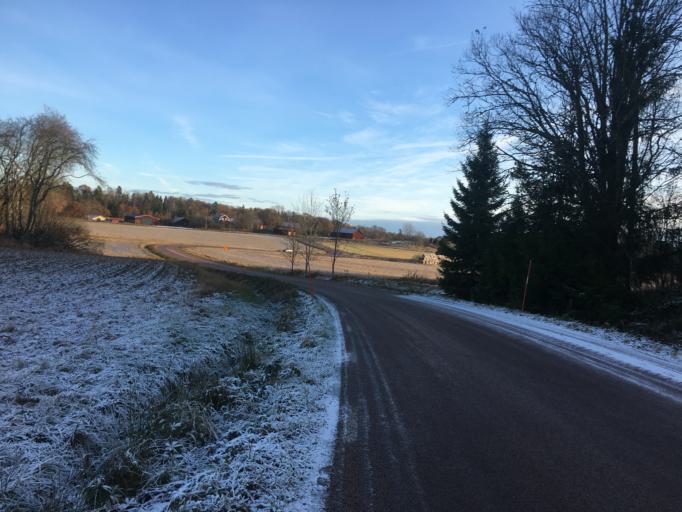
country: SE
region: Vaestmanland
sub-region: Vasteras
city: Vasteras
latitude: 59.6424
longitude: 16.4749
